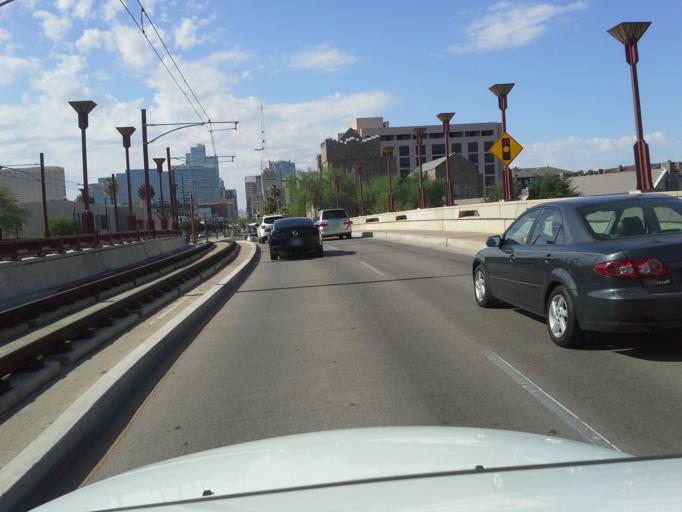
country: US
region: Arizona
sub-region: Maricopa County
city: Phoenix
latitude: 33.4619
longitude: -112.0739
